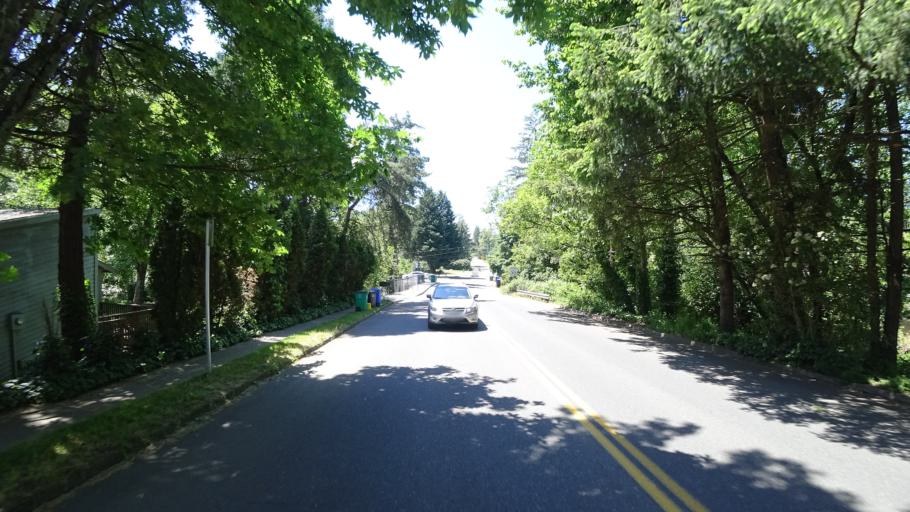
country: US
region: Oregon
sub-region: Washington County
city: Metzger
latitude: 45.4519
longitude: -122.7151
